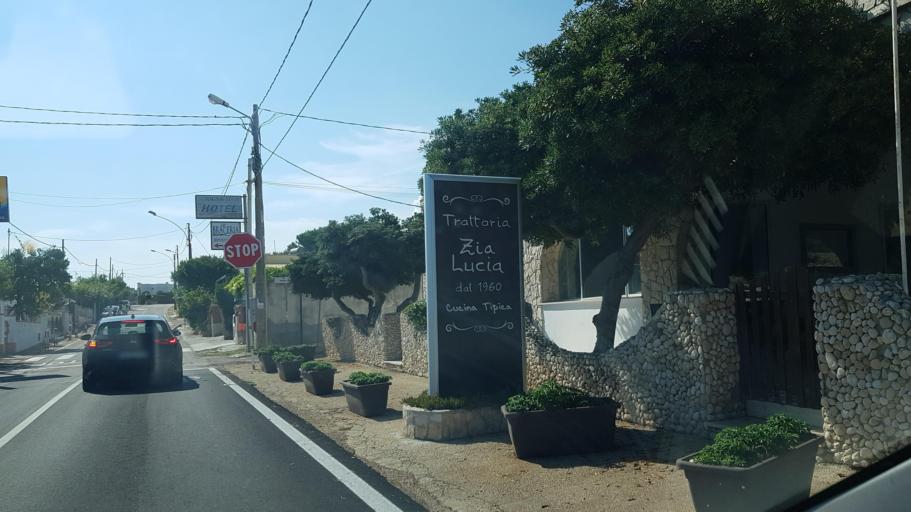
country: IT
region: Apulia
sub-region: Provincia di Lecce
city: Patu
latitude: 39.8110
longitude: 18.3194
